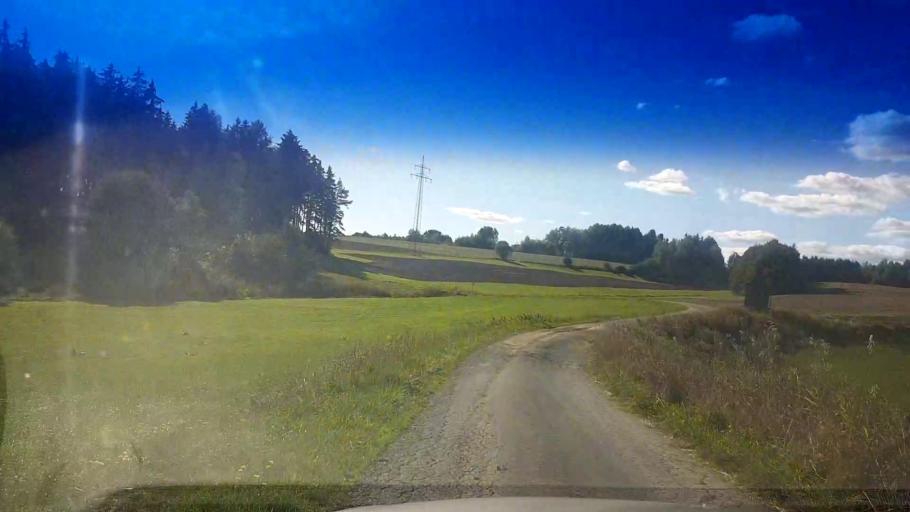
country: DE
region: Bavaria
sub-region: Upper Franconia
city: Thiersheim
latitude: 50.0336
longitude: 12.1235
